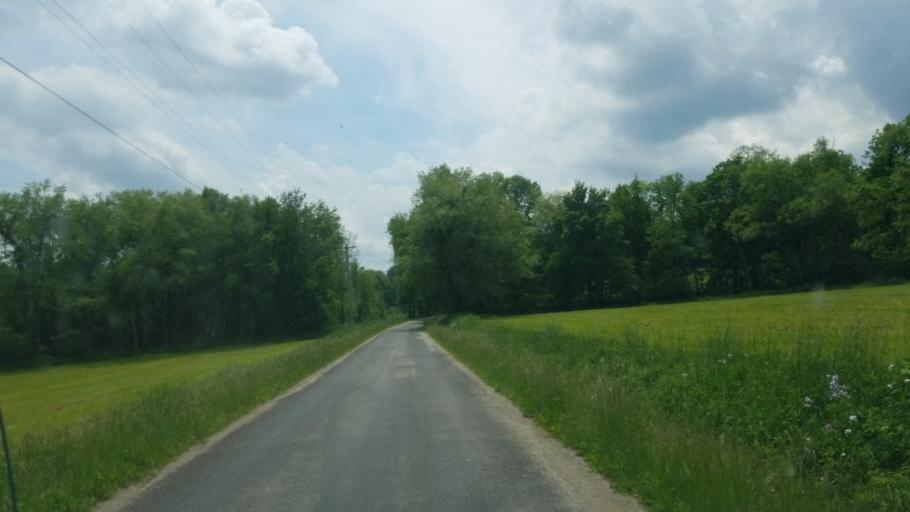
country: US
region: Ohio
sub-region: Ashland County
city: Ashland
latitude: 40.7678
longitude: -82.3420
